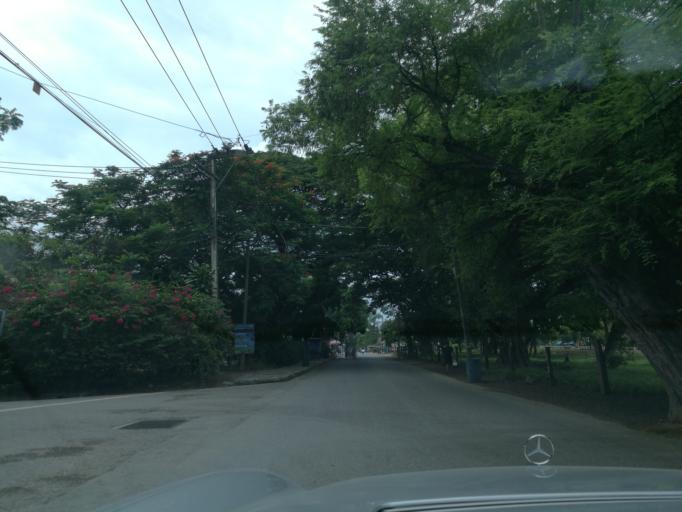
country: TH
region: Prachuap Khiri Khan
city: Prachuap Khiri Khan
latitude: 11.8093
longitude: 99.7936
